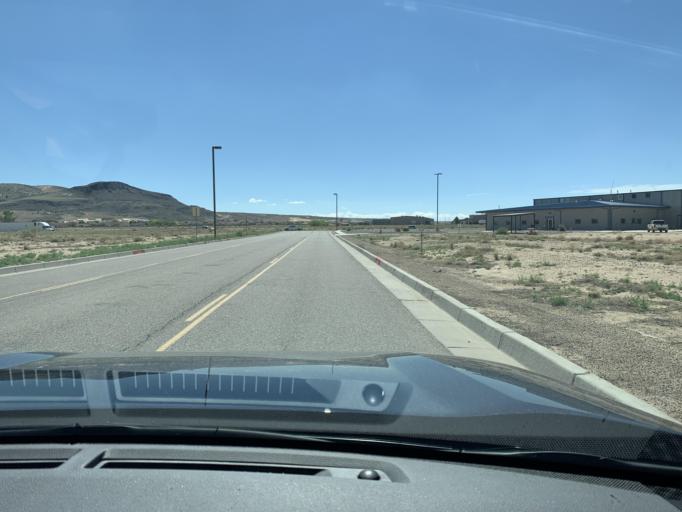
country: US
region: New Mexico
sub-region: Valencia County
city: Los Lunas
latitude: 34.8216
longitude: -106.7665
